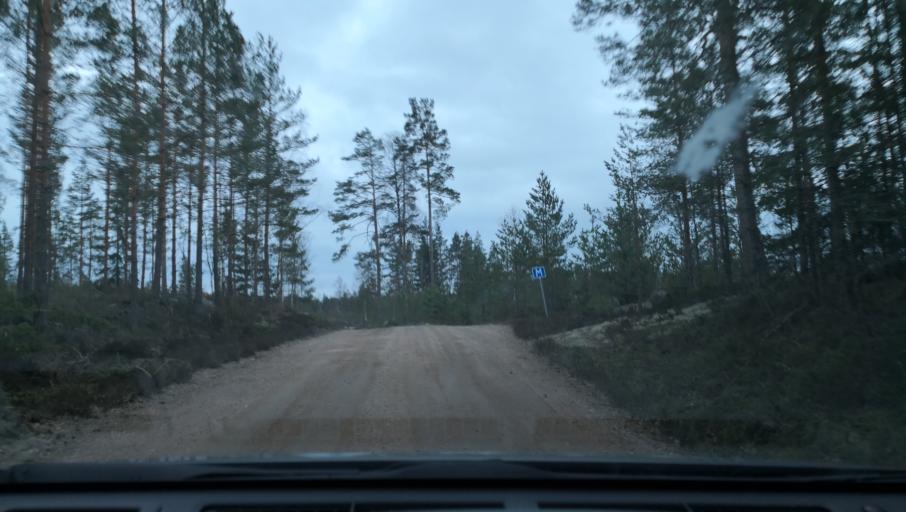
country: SE
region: OErebro
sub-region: Lindesbergs Kommun
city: Fellingsbro
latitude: 59.6067
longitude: 15.5767
